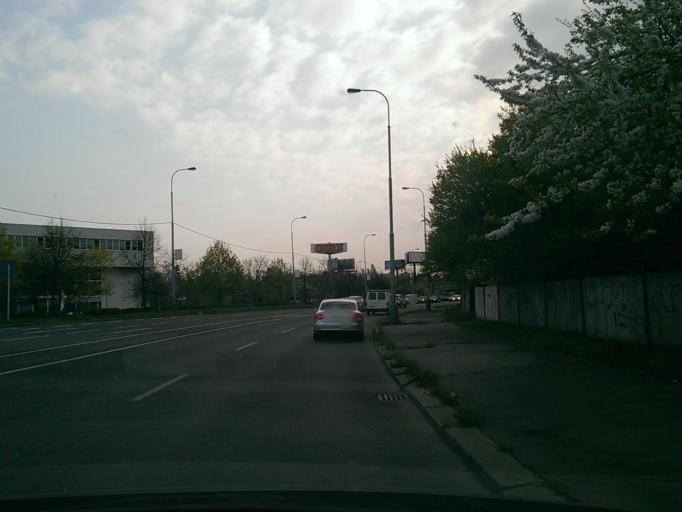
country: CZ
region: Praha
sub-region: Praha 4
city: Hodkovicky
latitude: 50.0384
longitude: 14.4794
